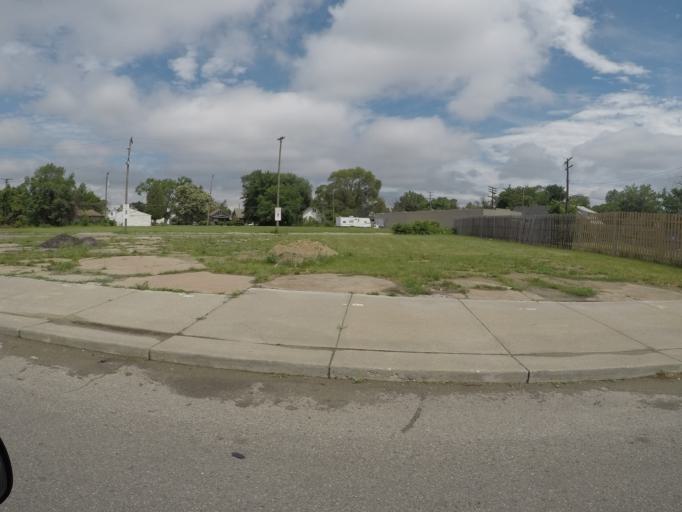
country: US
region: Michigan
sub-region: Wayne County
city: Dearborn
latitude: 42.3451
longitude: -83.1356
